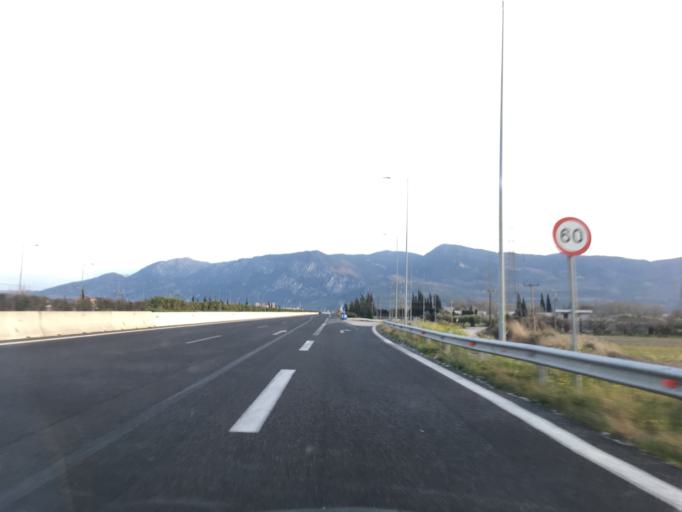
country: GR
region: Central Greece
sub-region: Nomos Fthiotidos
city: Anthili
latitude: 38.8518
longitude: 22.4684
